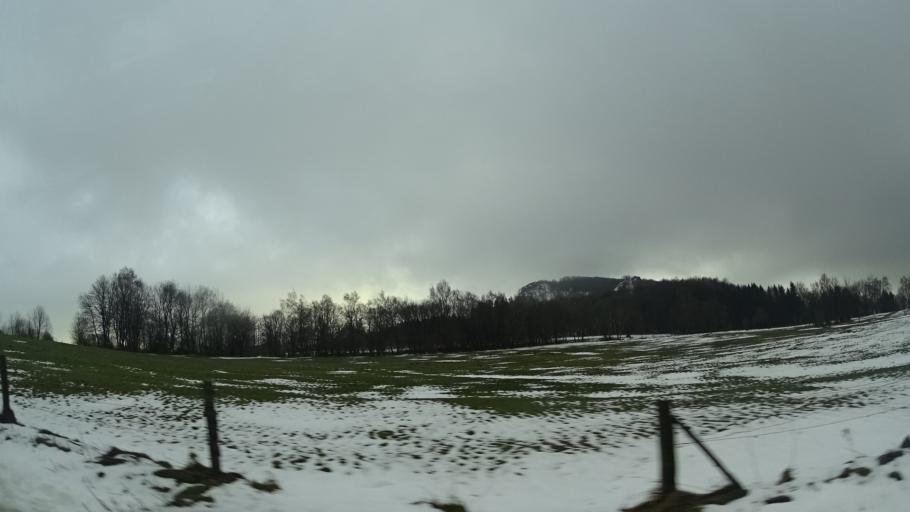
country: DE
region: Hesse
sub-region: Regierungsbezirk Kassel
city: Hofbieber
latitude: 50.5531
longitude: 9.8949
